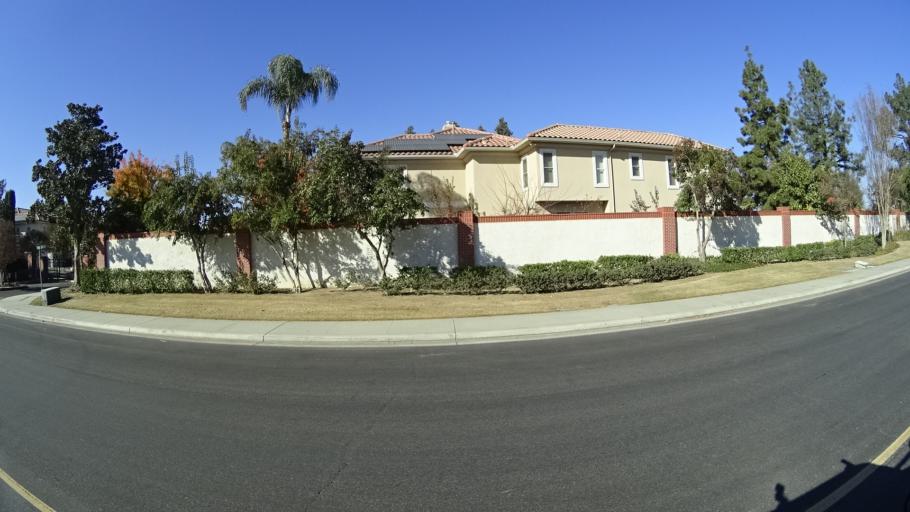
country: US
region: California
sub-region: Kern County
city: Greenacres
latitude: 35.3290
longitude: -119.1176
